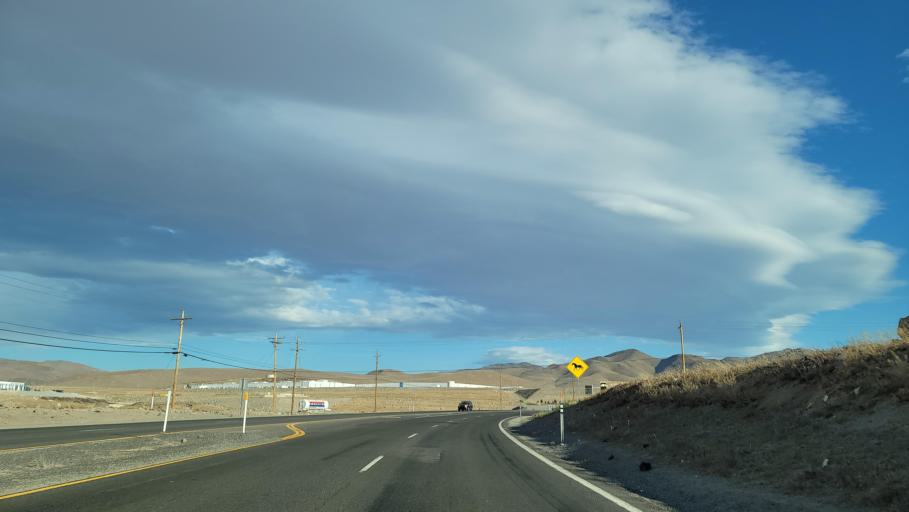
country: US
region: Nevada
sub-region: Lyon County
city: Stagecoach
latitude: 39.5475
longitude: -119.4852
